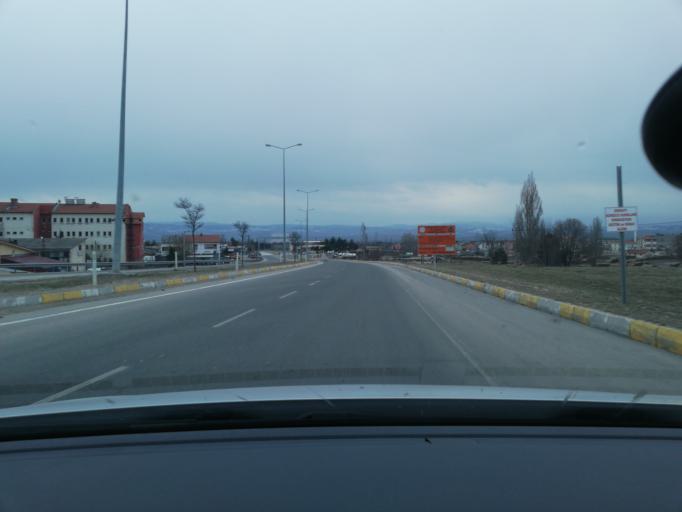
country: TR
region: Bolu
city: Gerede
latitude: 40.7910
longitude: 32.2082
